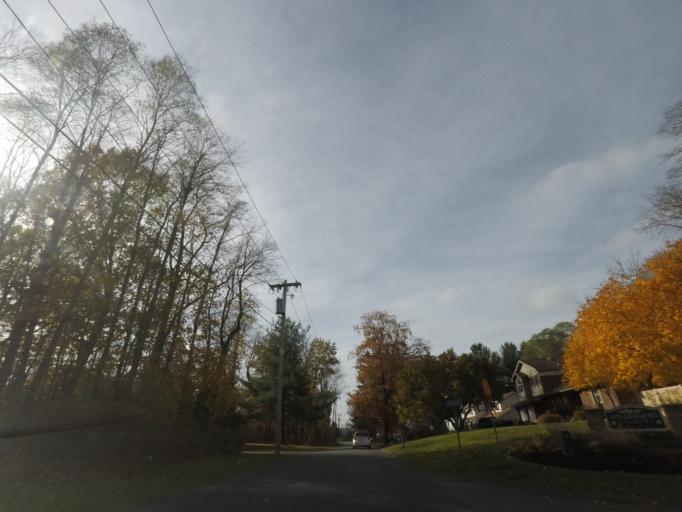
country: US
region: New York
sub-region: Schenectady County
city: Rotterdam
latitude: 42.7572
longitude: -73.9643
